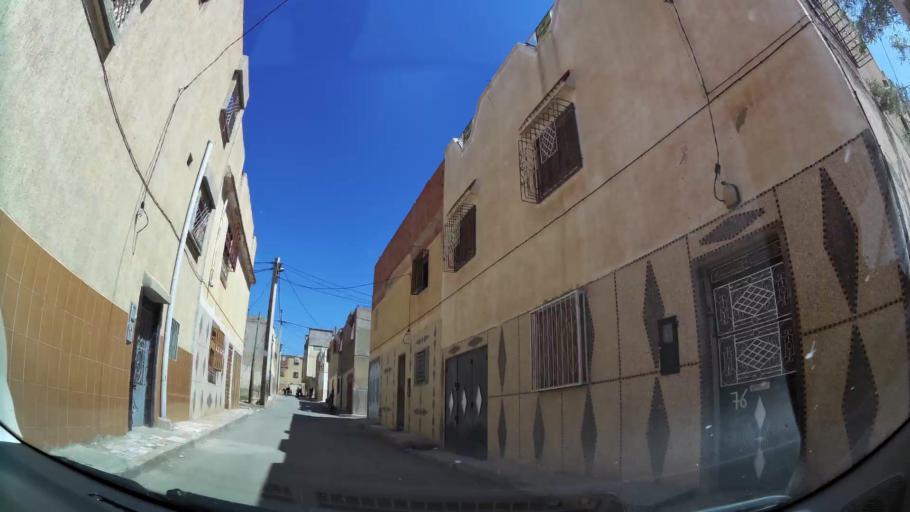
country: MA
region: Oriental
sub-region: Oujda-Angad
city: Oujda
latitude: 34.6894
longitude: -1.9328
